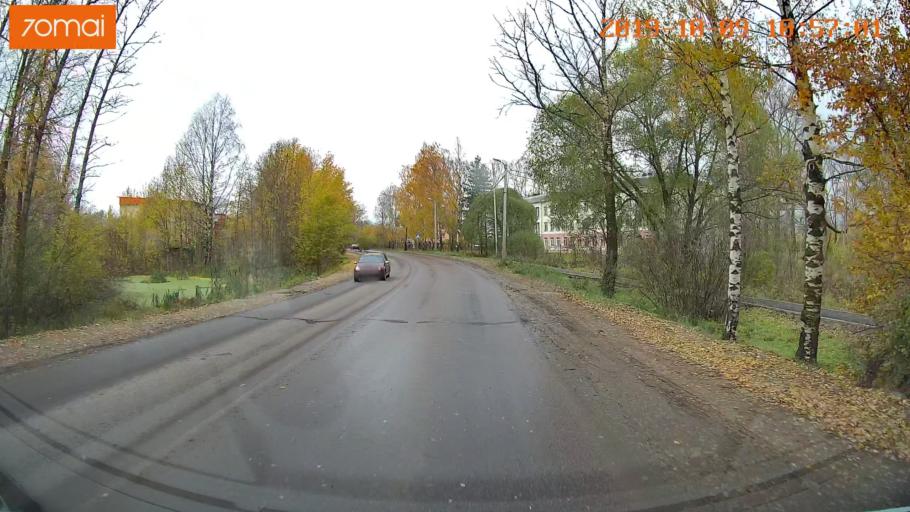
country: RU
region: Vologda
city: Vologda
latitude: 59.2380
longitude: 39.8134
